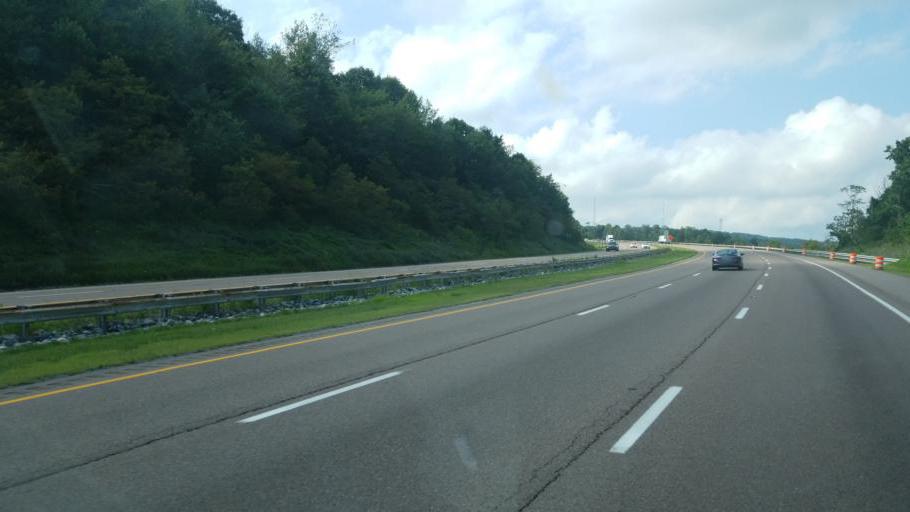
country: US
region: Maryland
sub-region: Allegany County
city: Frostburg
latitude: 39.6557
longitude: -78.9538
